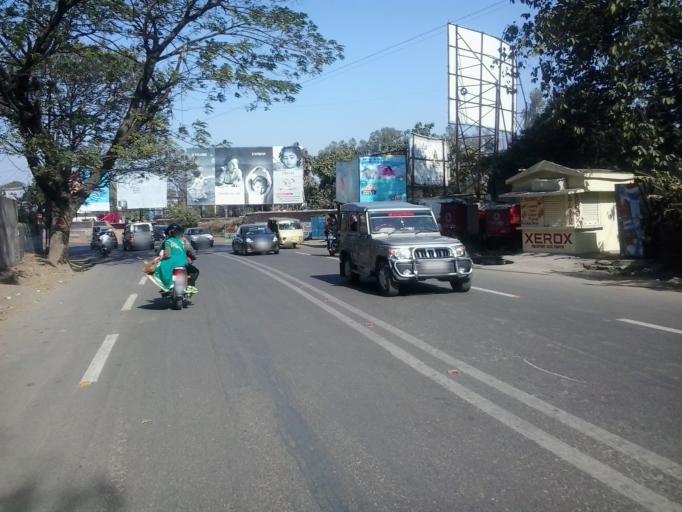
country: IN
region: Jharkhand
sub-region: Ranchi
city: Ranchi
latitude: 23.3431
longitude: 85.3211
